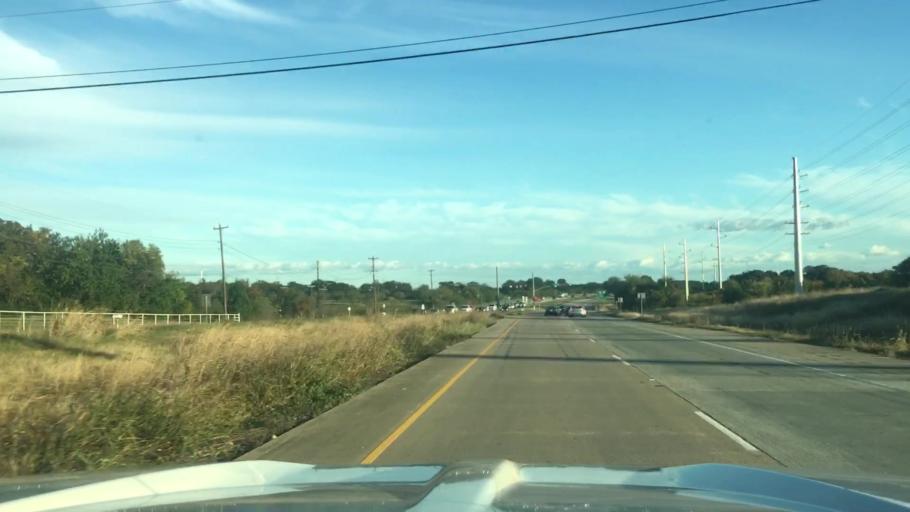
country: US
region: Texas
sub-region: Denton County
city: Denton
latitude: 33.2495
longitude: -97.0966
